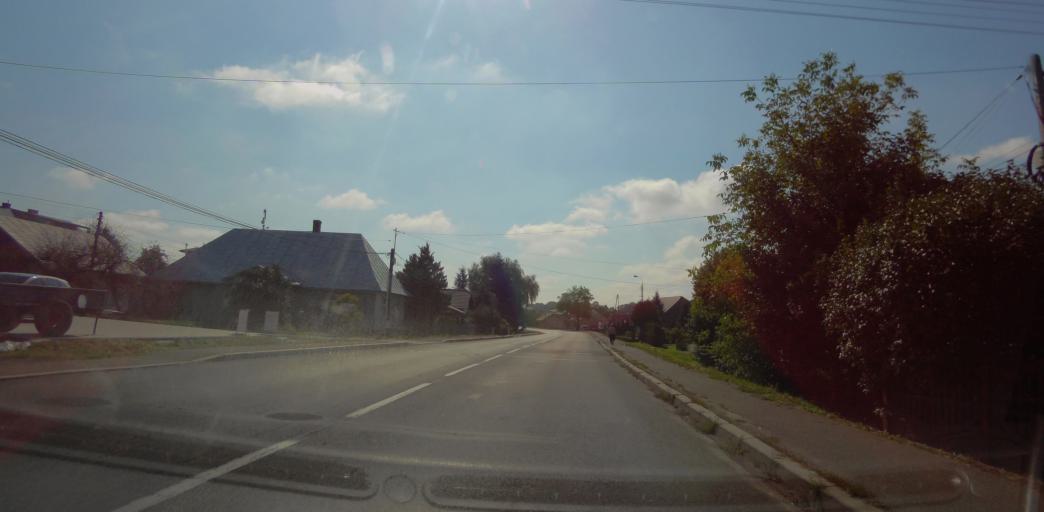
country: PL
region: Subcarpathian Voivodeship
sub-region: Powiat brzozowski
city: Humniska
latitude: 49.6791
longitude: 22.0466
